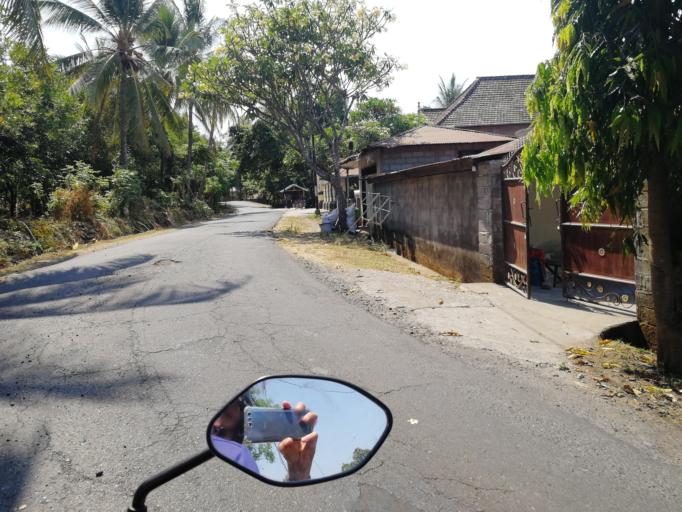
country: ID
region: Bali
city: Banjar Trunyan
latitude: -8.1265
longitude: 115.3291
